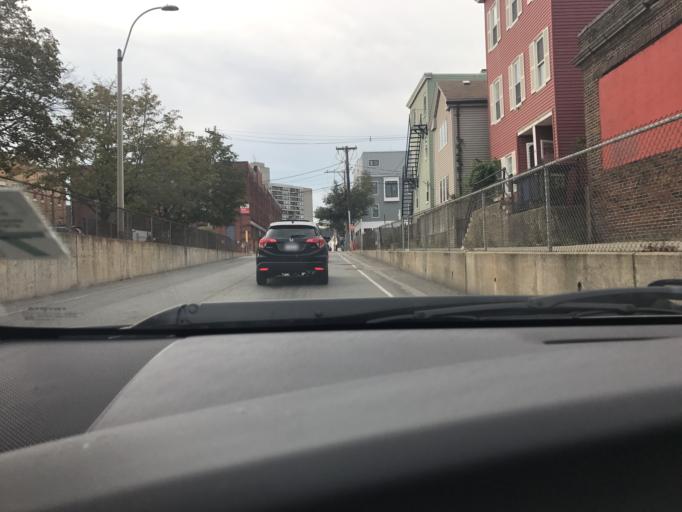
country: US
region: Massachusetts
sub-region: Middlesex County
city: Somerville
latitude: 42.3754
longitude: -71.0886
